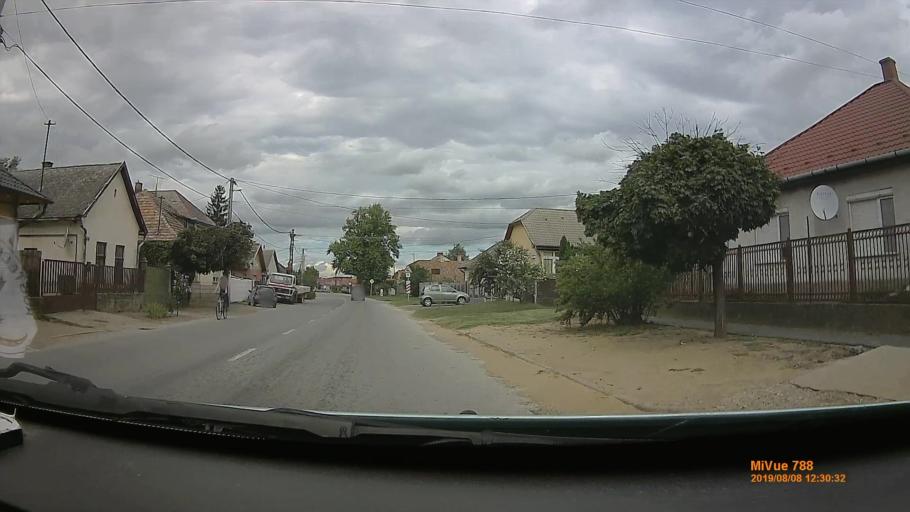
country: HU
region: Szabolcs-Szatmar-Bereg
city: Nyirbator
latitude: 47.8400
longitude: 22.1227
